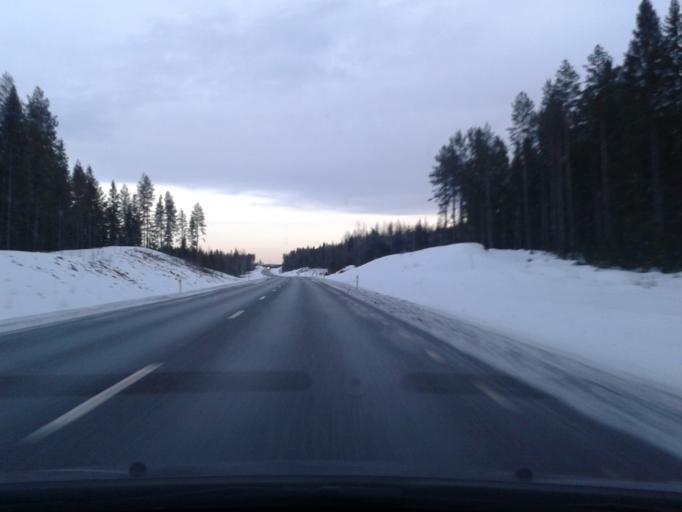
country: SE
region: Vaesternorrland
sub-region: Kramfors Kommun
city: Bollstabruk
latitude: 63.0696
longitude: 17.5723
